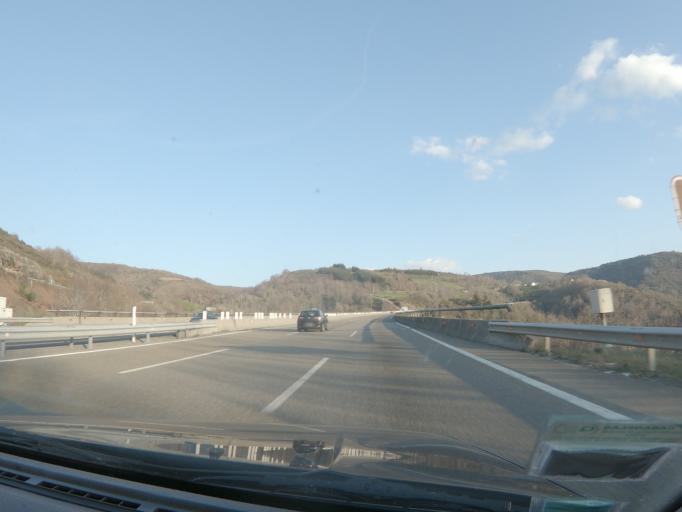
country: ES
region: Galicia
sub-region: Provincia de Lugo
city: San Roman
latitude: 42.7437
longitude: -7.0525
